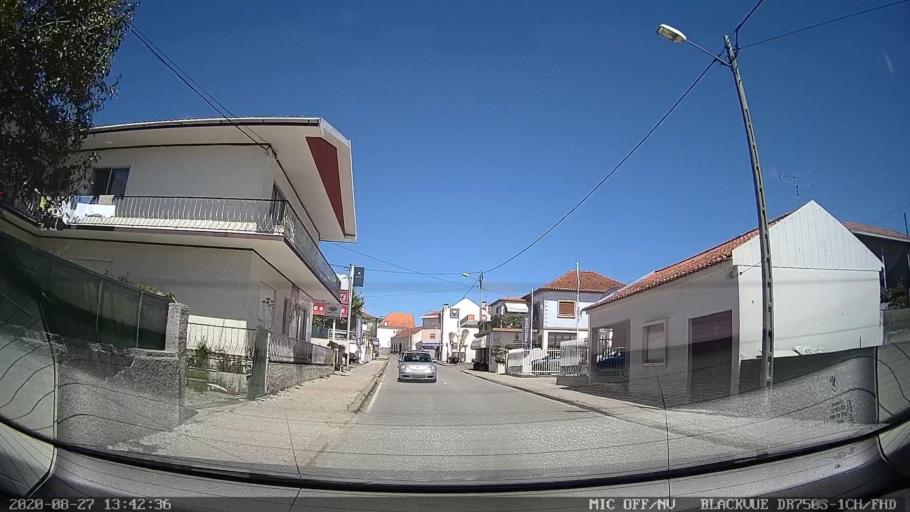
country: PT
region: Coimbra
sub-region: Mira
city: Mira
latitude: 40.4260
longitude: -8.7367
